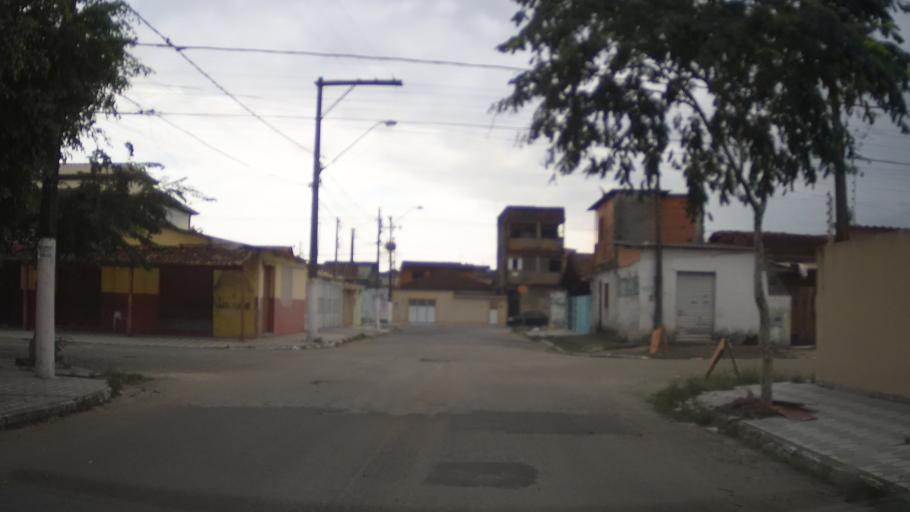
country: BR
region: Sao Paulo
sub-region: Praia Grande
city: Praia Grande
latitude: -24.0067
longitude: -46.4420
